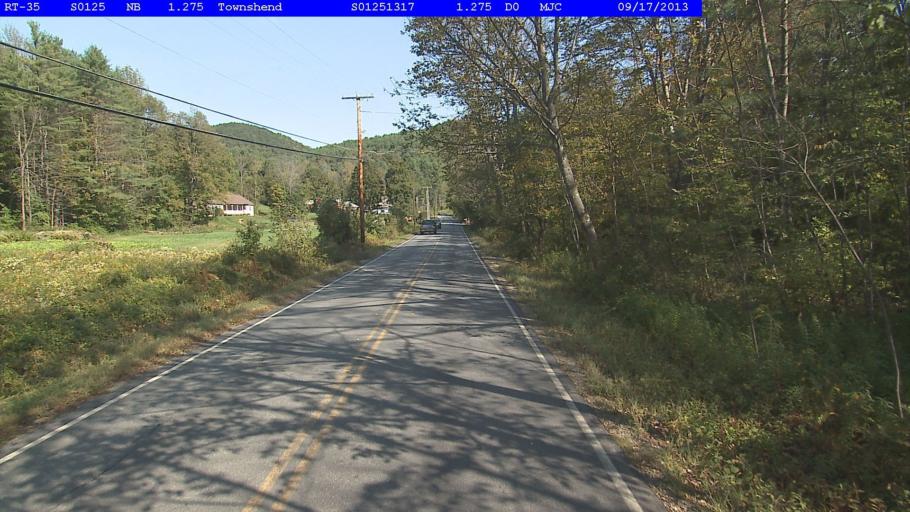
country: US
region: Vermont
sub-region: Windham County
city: Newfane
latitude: 43.0639
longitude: -72.6614
